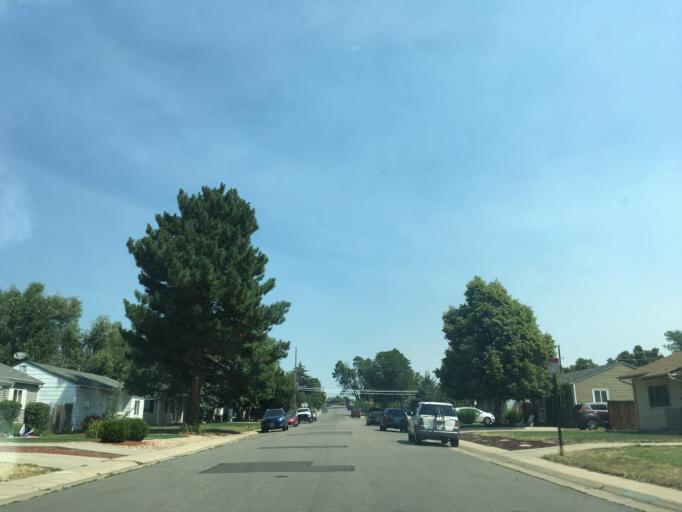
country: US
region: Colorado
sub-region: Jefferson County
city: Lakewood
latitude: 39.6939
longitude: -105.0507
